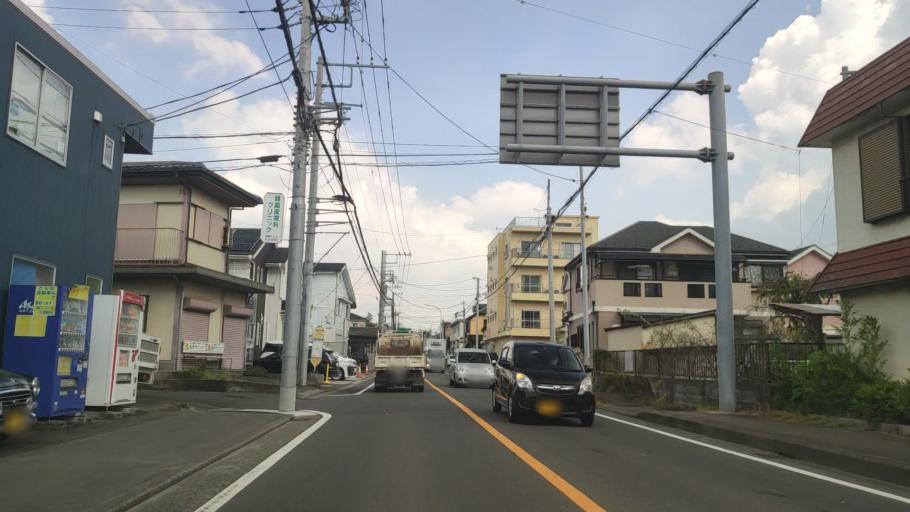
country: JP
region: Kanagawa
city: Minami-rinkan
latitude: 35.4477
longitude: 139.5042
